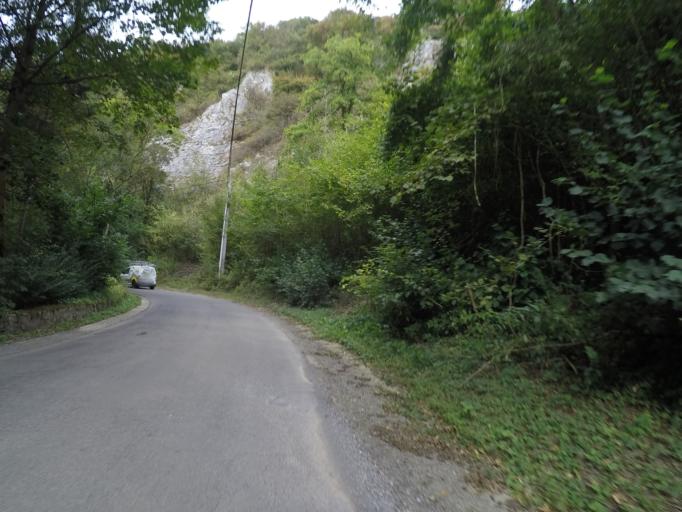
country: BE
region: Wallonia
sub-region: Province de Namur
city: Dinant
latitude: 50.2748
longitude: 4.9542
